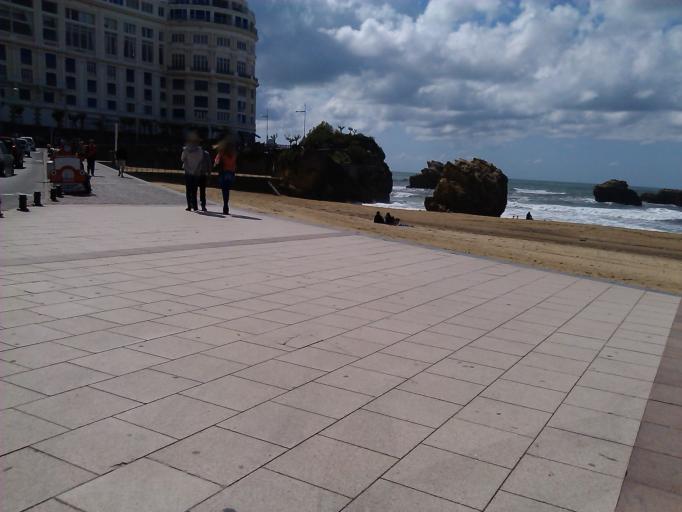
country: FR
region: Aquitaine
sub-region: Departement des Pyrenees-Atlantiques
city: Biarritz
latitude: 43.4834
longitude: -1.5605
